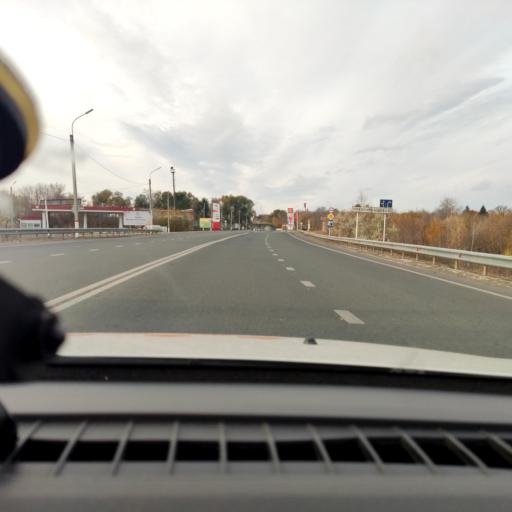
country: RU
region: Samara
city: Novokuybyshevsk
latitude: 53.1217
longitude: 49.9428
